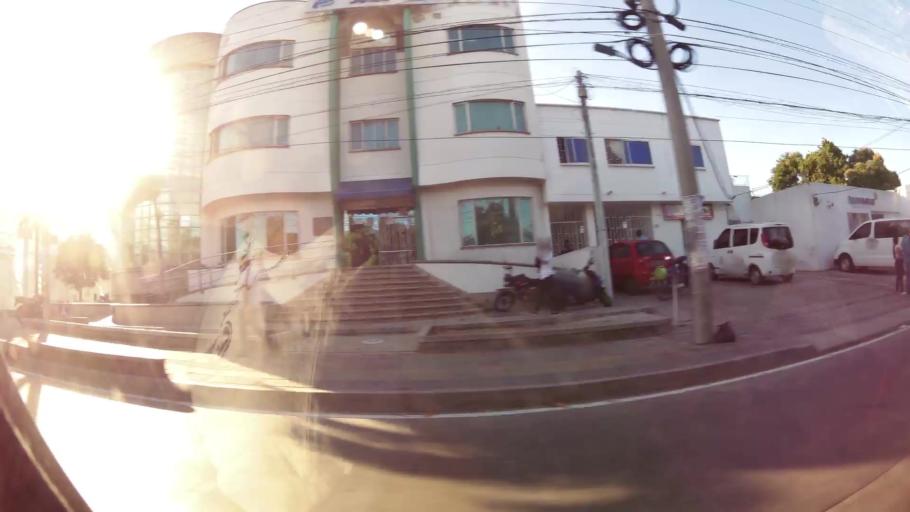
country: CO
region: Atlantico
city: Barranquilla
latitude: 10.9509
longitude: -74.7997
